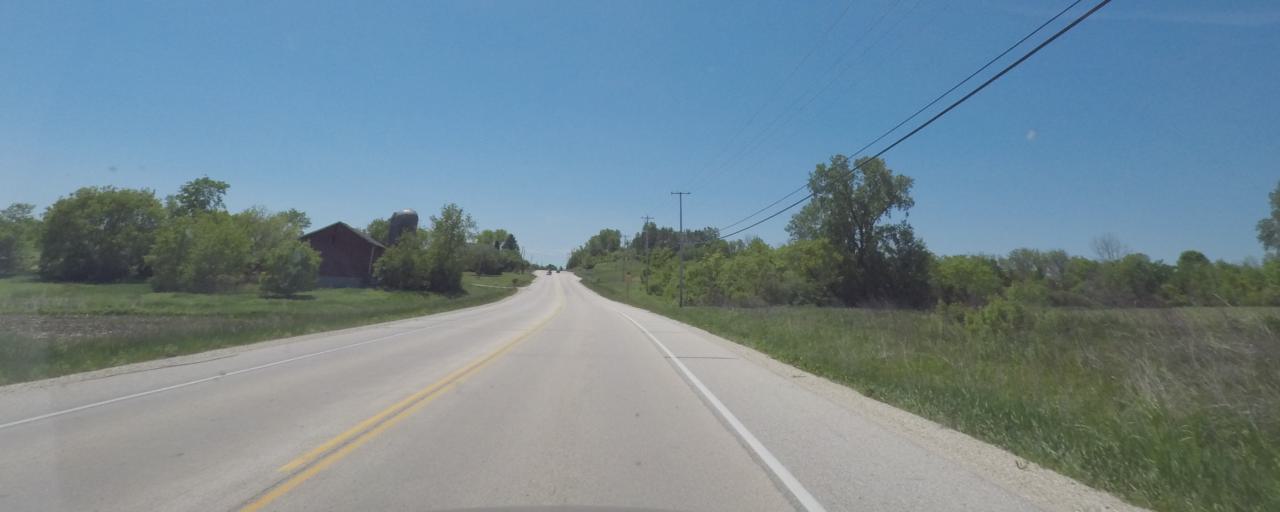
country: US
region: Wisconsin
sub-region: Washington County
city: West Bend
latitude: 43.4598
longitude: -88.1585
